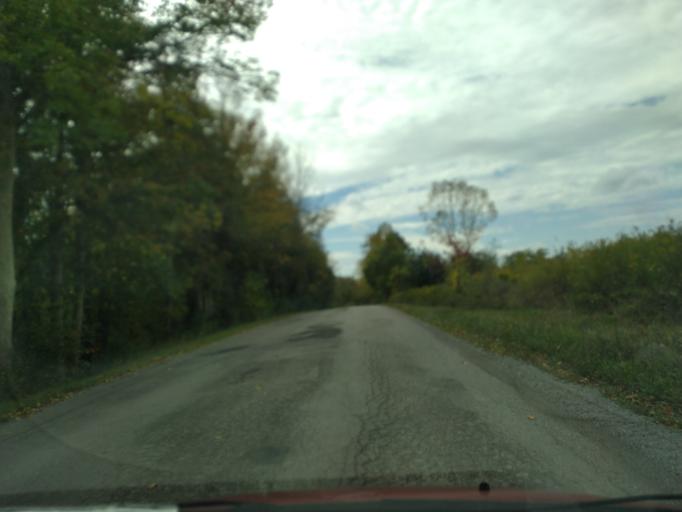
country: CA
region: Ontario
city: Keswick
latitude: 44.2610
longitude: -79.3478
